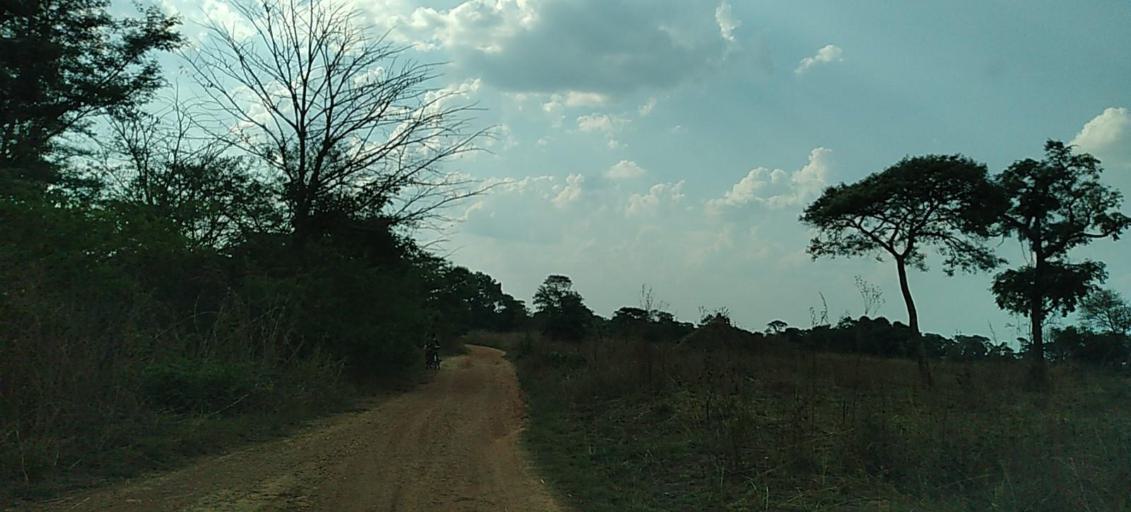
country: ZM
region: Copperbelt
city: Mpongwe
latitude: -13.5120
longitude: 28.0964
